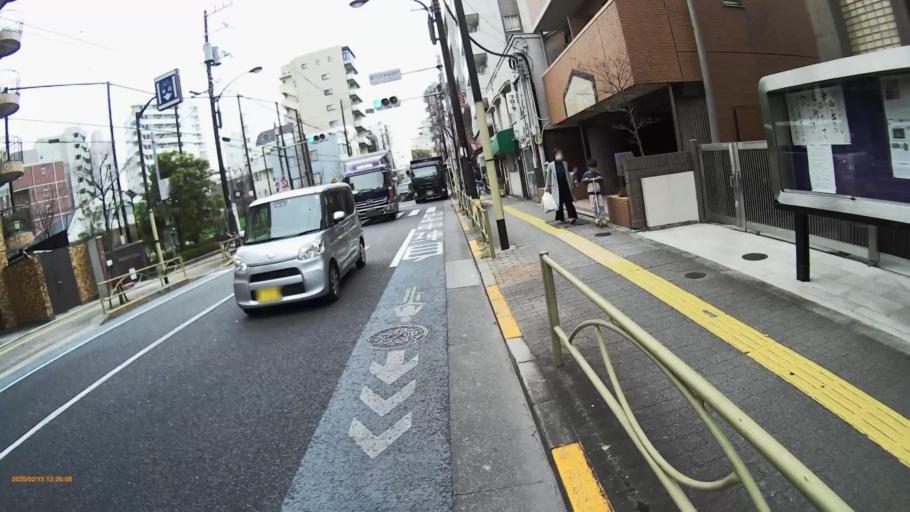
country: JP
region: Tokyo
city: Tokyo
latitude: 35.7169
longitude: 139.7565
